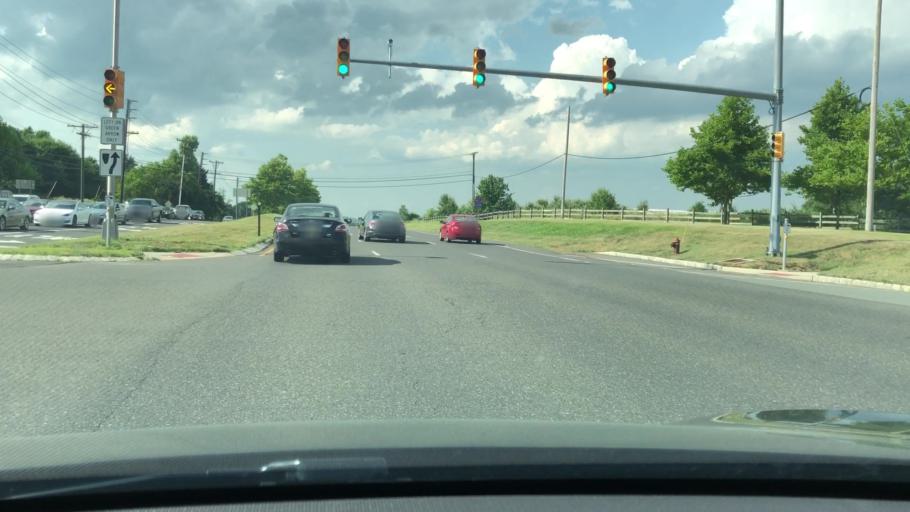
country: US
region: New Jersey
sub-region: Mercer County
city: Ewing
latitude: 40.2948
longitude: -74.8111
